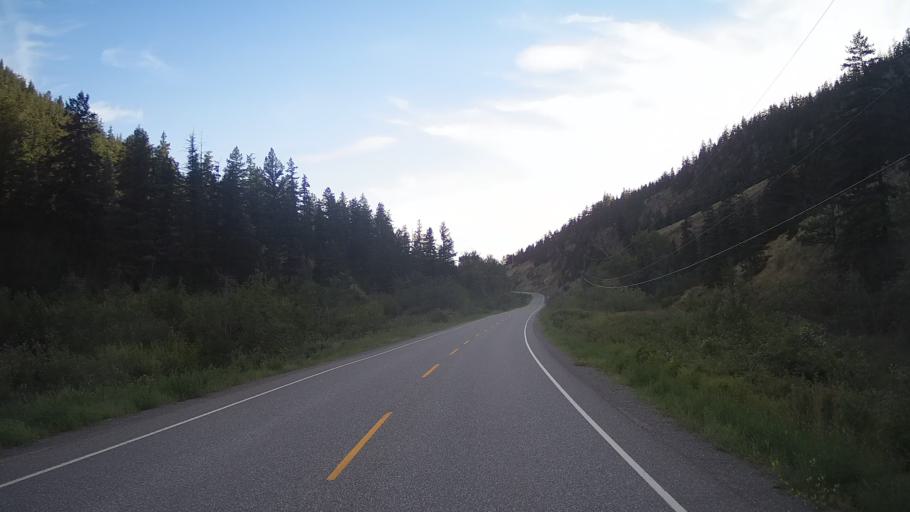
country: CA
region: British Columbia
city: Cache Creek
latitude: 50.8716
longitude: -121.5217
